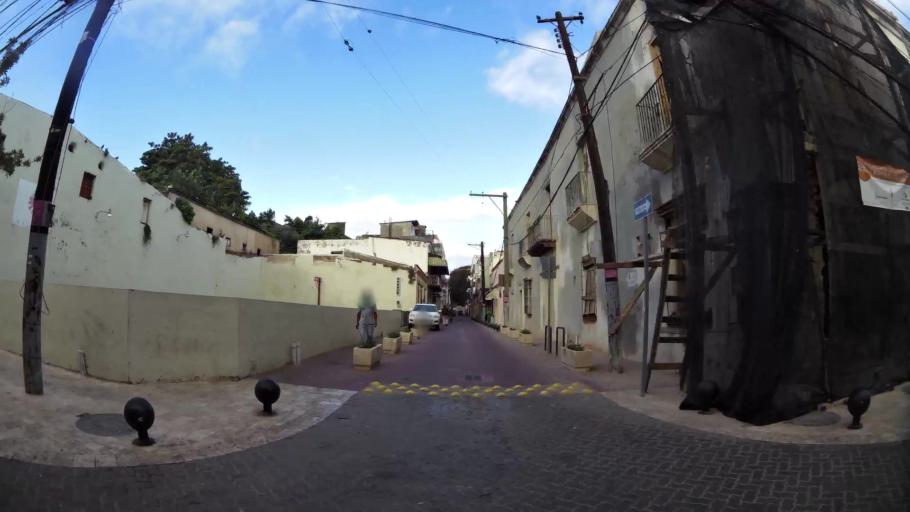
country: DO
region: Nacional
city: Ciudad Nueva
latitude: 18.4748
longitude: -69.8839
